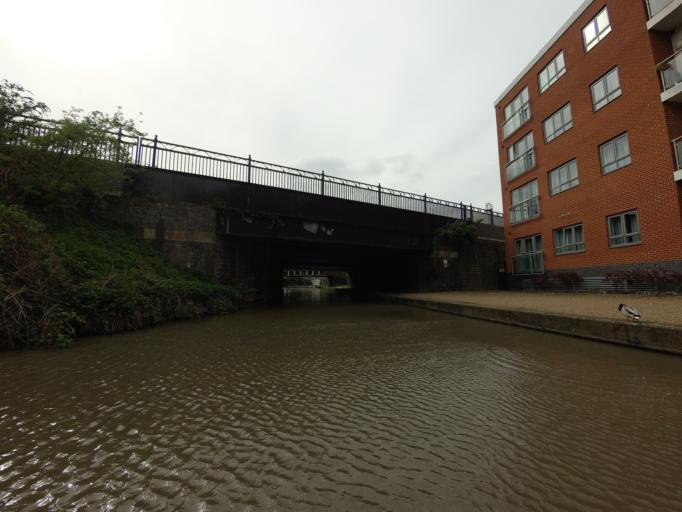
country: GB
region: England
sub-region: Milton Keynes
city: Bradwell
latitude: 52.0652
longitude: -0.8066
